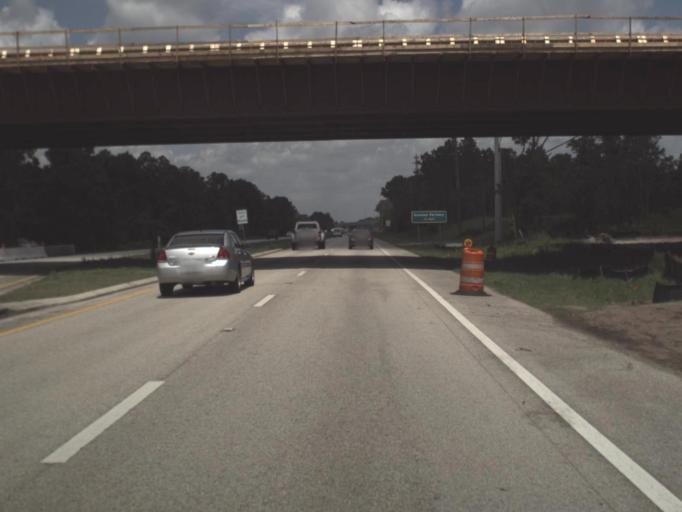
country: US
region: Florida
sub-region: Saint Johns County
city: Palm Valley
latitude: 30.0899
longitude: -81.4638
